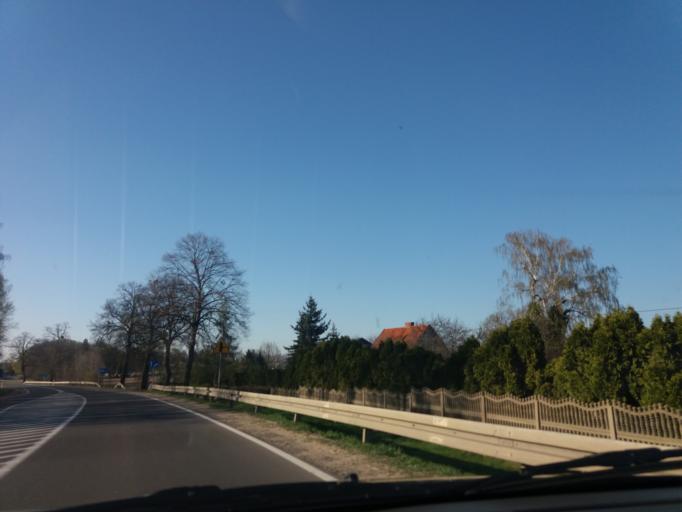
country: PL
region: Warmian-Masurian Voivodeship
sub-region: Powiat nidzicki
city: Nidzica
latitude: 53.3455
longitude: 20.4332
